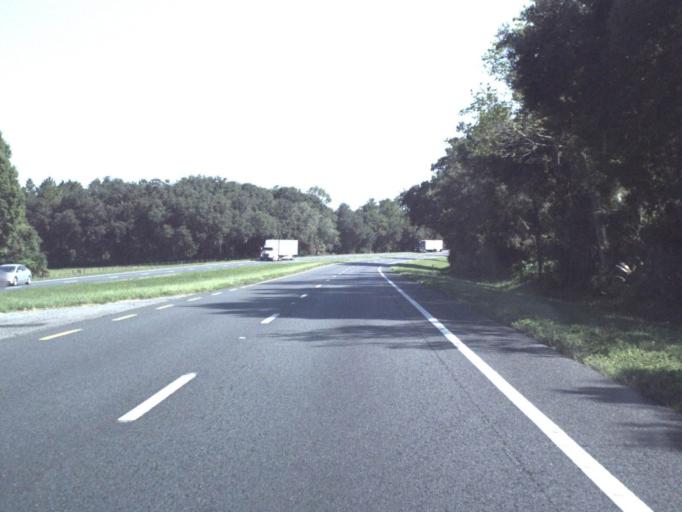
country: US
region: Florida
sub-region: Marion County
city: Citra
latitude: 29.4607
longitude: -82.1094
